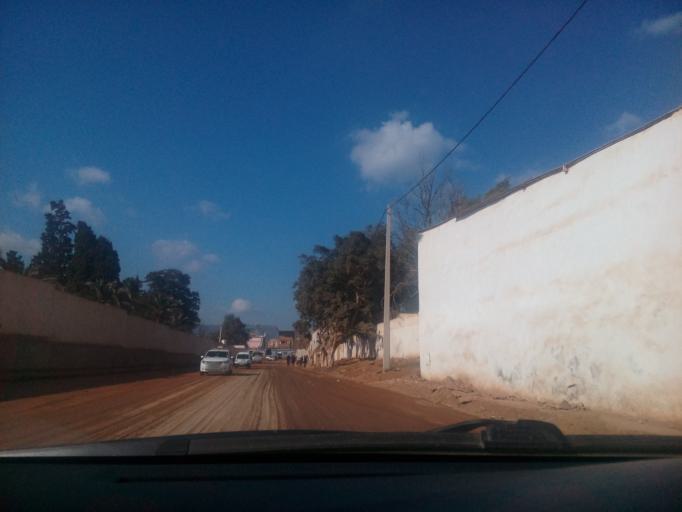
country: DZ
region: Oran
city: Oran
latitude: 35.6808
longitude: -0.6080
